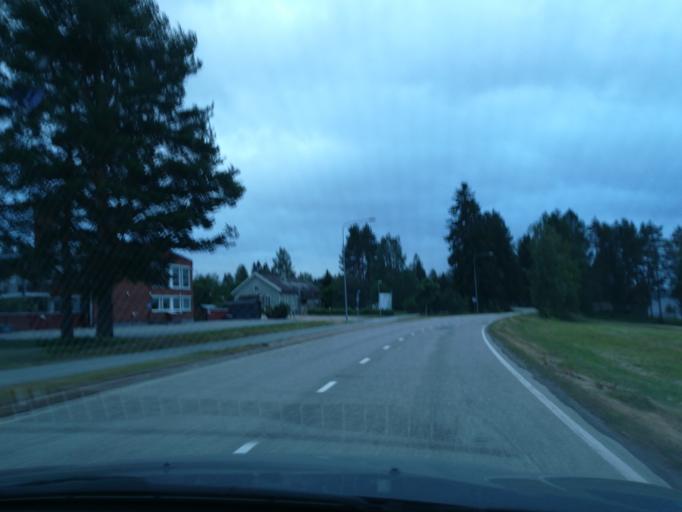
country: FI
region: Southern Savonia
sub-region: Mikkeli
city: Ristiina
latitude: 61.5036
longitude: 27.2653
